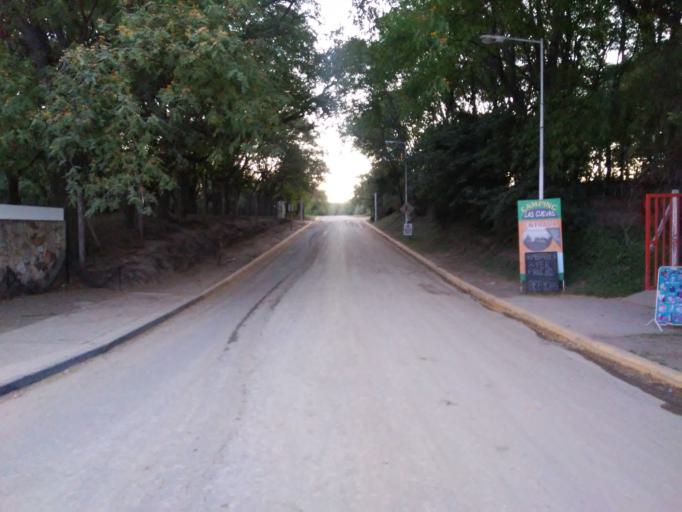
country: AR
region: Buenos Aires
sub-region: Partido de San Pedro
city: San Pedro
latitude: -33.5966
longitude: -59.8108
